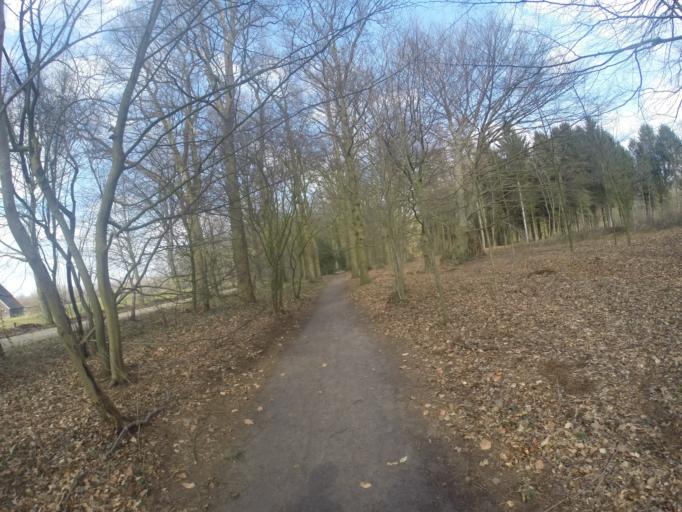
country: NL
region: Gelderland
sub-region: Gemeente Lochem
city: Almen
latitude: 52.1207
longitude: 6.3084
